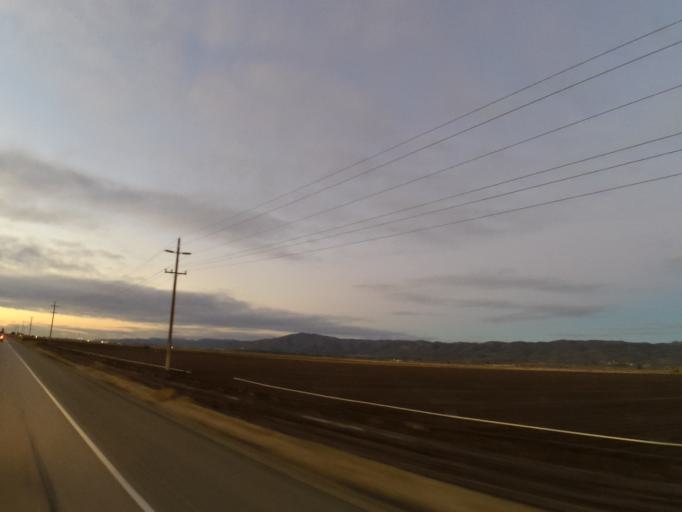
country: US
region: California
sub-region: Monterey County
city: Greenfield
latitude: 36.3679
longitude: -121.2820
